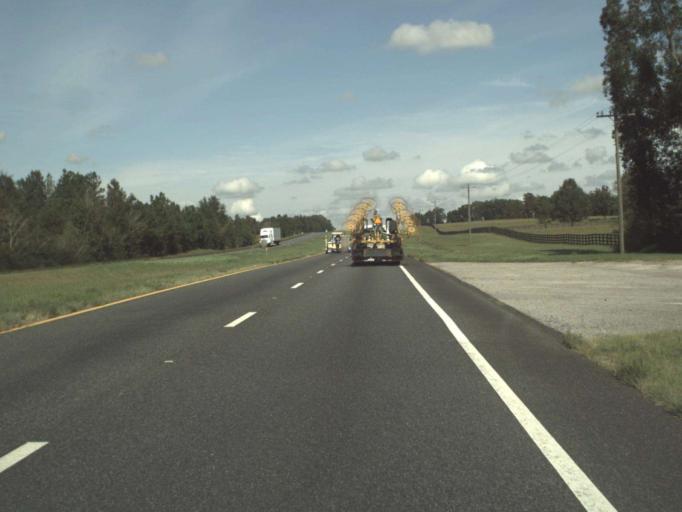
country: US
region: Florida
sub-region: Jackson County
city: Graceville
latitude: 30.8808
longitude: -85.3645
